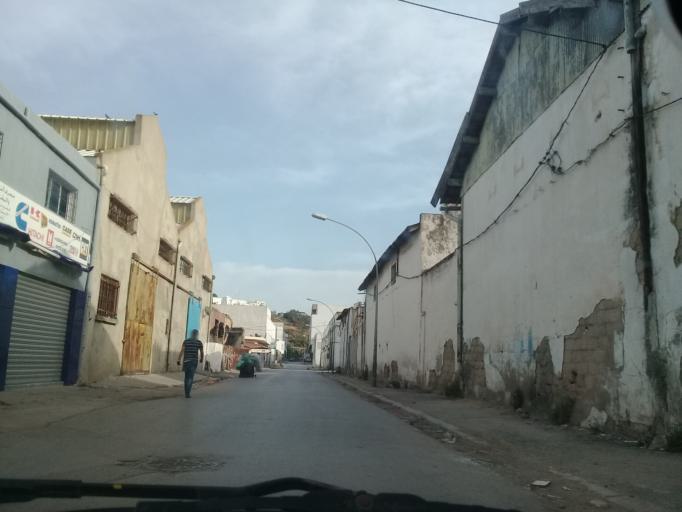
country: TN
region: Tunis
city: Tunis
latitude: 36.7919
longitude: 10.1856
